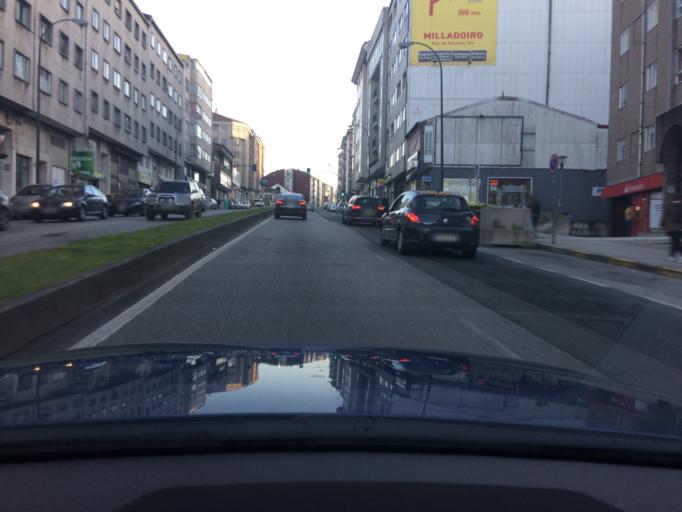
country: ES
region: Galicia
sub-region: Provincia da Coruna
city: Santiago de Compostela
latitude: 42.8445
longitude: -8.5767
